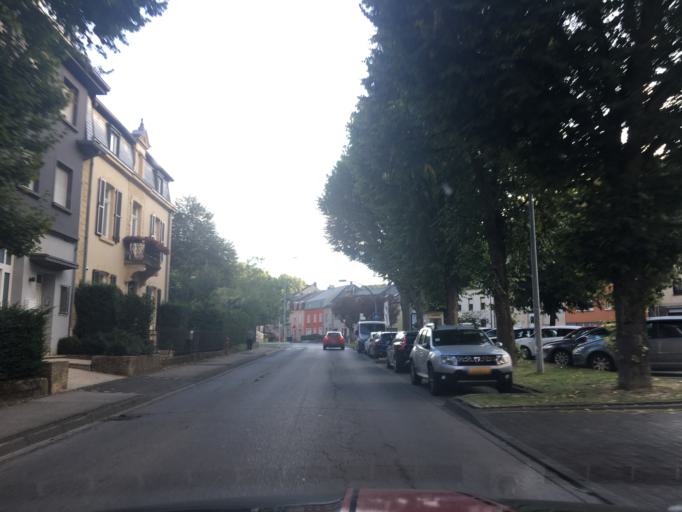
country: LU
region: Luxembourg
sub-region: Canton d'Esch-sur-Alzette
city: Differdange
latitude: 49.5209
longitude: 5.8827
